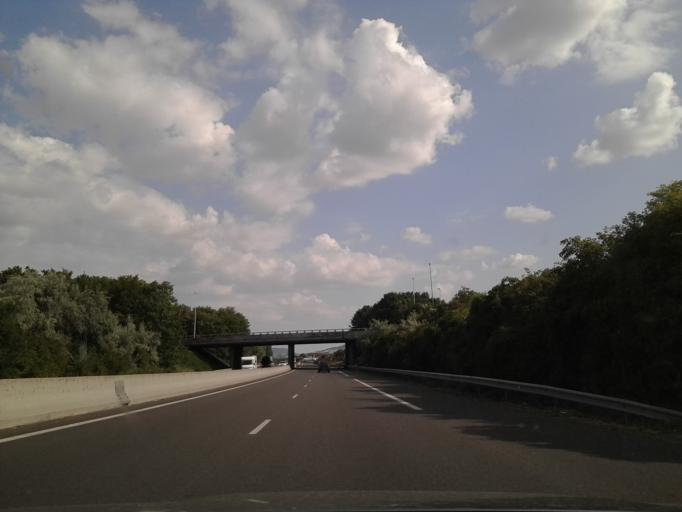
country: FR
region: Auvergne
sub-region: Departement du Puy-de-Dome
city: Perignat-les-Sarlieve
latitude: 45.7610
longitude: 3.1393
